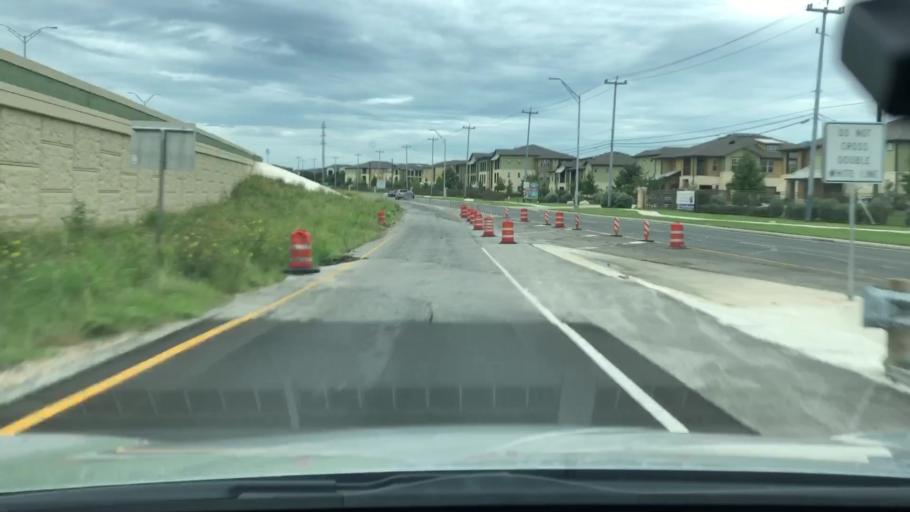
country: US
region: Texas
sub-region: Bexar County
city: Leon Valley
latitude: 29.4453
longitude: -98.6663
